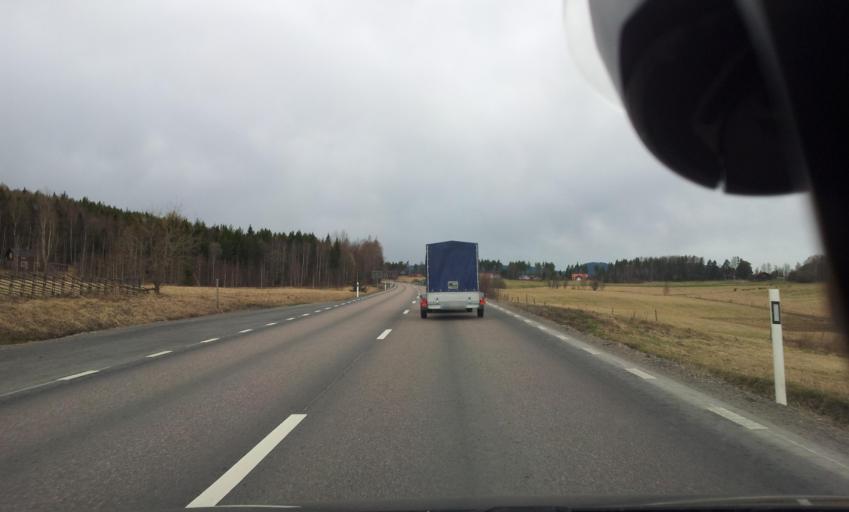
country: SE
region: Gaevleborg
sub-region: Ljusdals Kommun
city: Ljusdal
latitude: 61.8233
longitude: 16.0503
